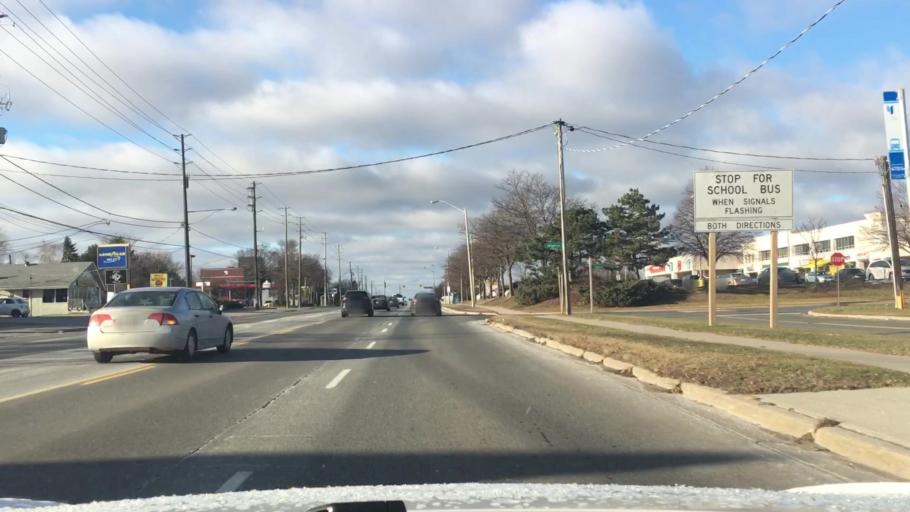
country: CA
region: Ontario
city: Markham
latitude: 43.8720
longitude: -79.2651
